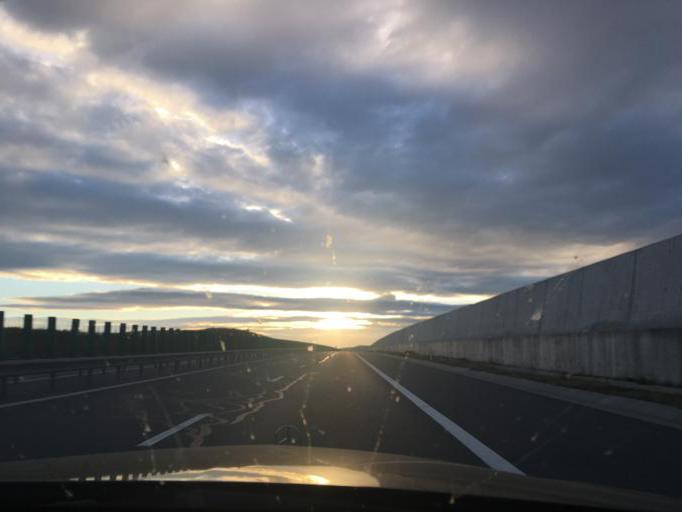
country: RO
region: Cluj
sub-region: Comuna Petrestii De Jos
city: Petrestii de Jos
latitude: 46.6002
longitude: 23.6708
